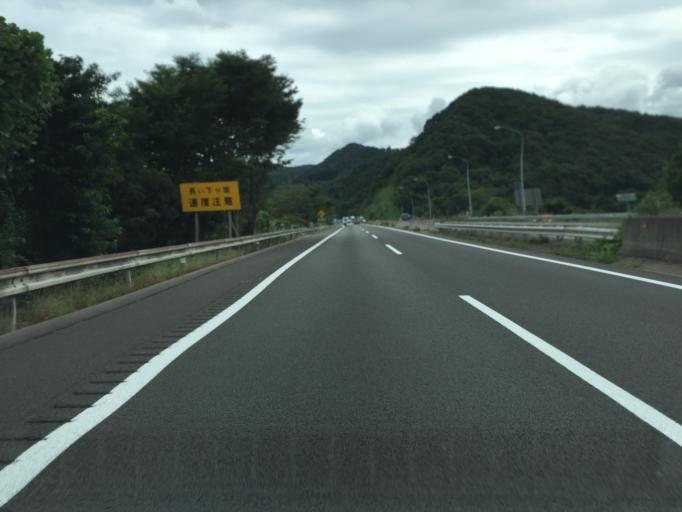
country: JP
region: Fukushima
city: Yanagawamachi-saiwaicho
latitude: 37.9114
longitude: 140.5885
